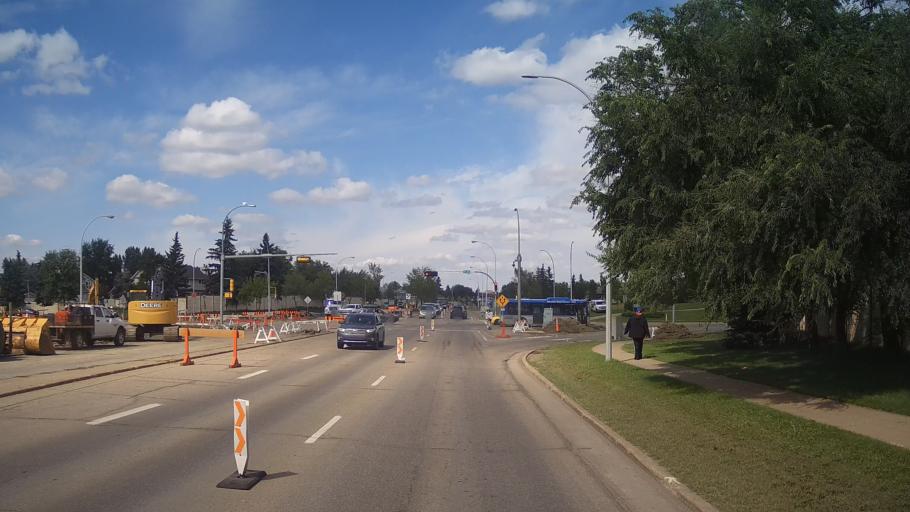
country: CA
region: Alberta
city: St. Albert
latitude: 53.5277
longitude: -113.6298
